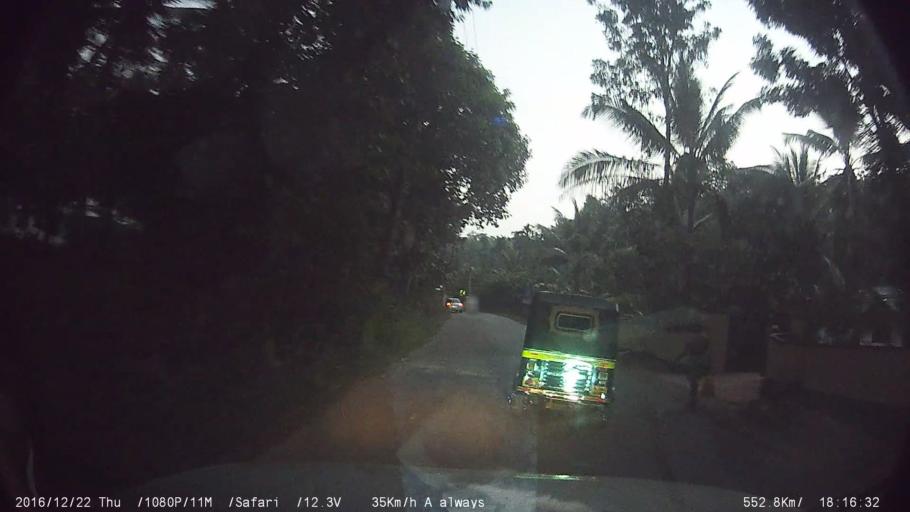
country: IN
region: Kerala
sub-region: Kottayam
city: Palackattumala
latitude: 9.7682
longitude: 76.6104
